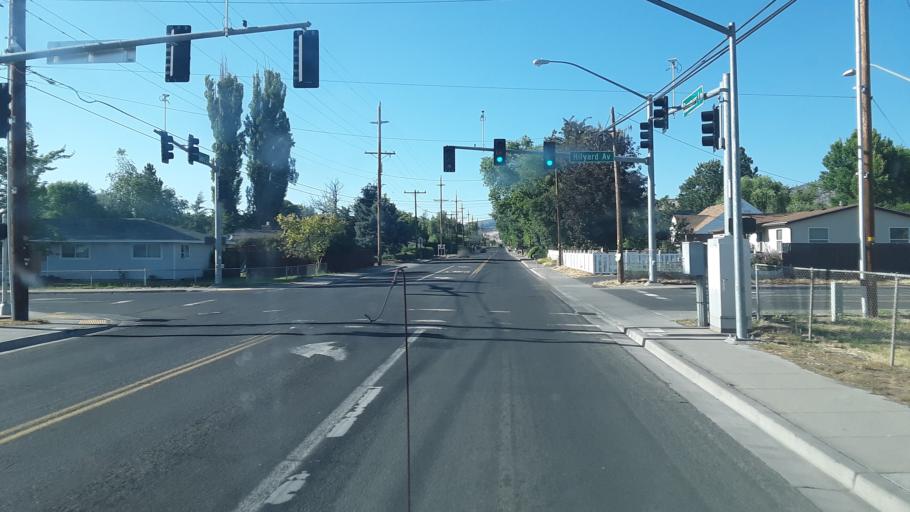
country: US
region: Oregon
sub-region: Klamath County
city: Altamont
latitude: 42.1990
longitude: -121.7377
